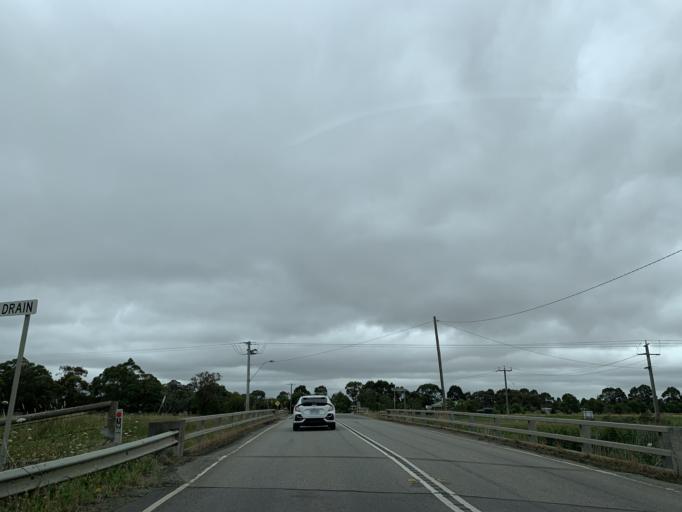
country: AU
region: Victoria
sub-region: Cardinia
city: Pakenham South
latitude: -38.1612
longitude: 145.5345
